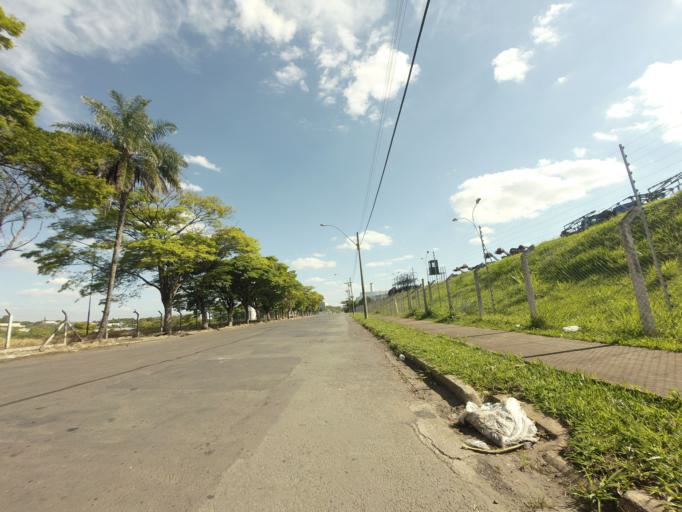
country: BR
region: Sao Paulo
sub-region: Piracicaba
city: Piracicaba
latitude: -22.7245
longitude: -47.5952
